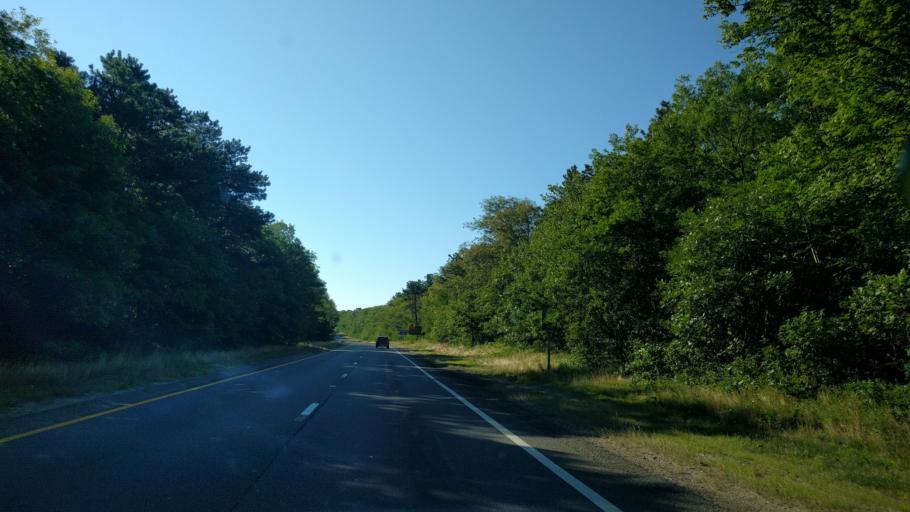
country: US
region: Massachusetts
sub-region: Barnstable County
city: West Barnstable
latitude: 41.6912
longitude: -70.3760
